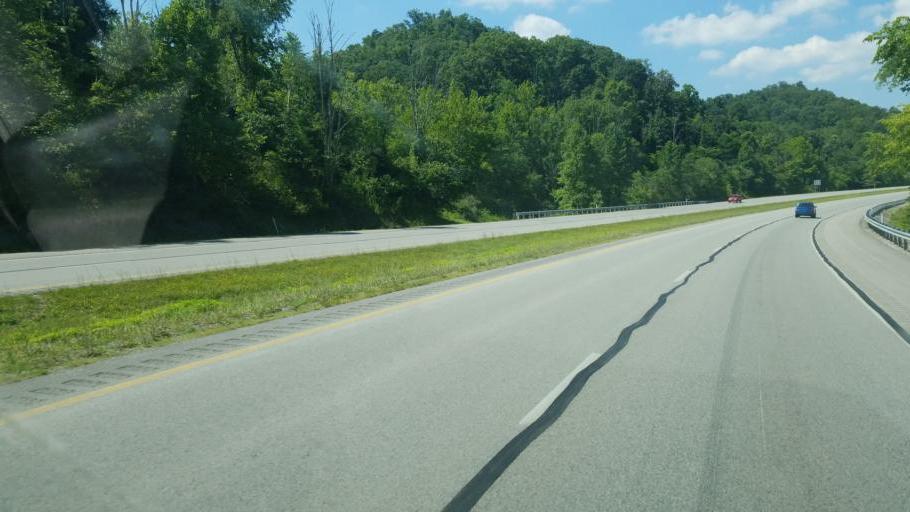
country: US
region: West Virginia
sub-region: Kanawha County
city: Sissonville
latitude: 38.5767
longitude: -81.6414
